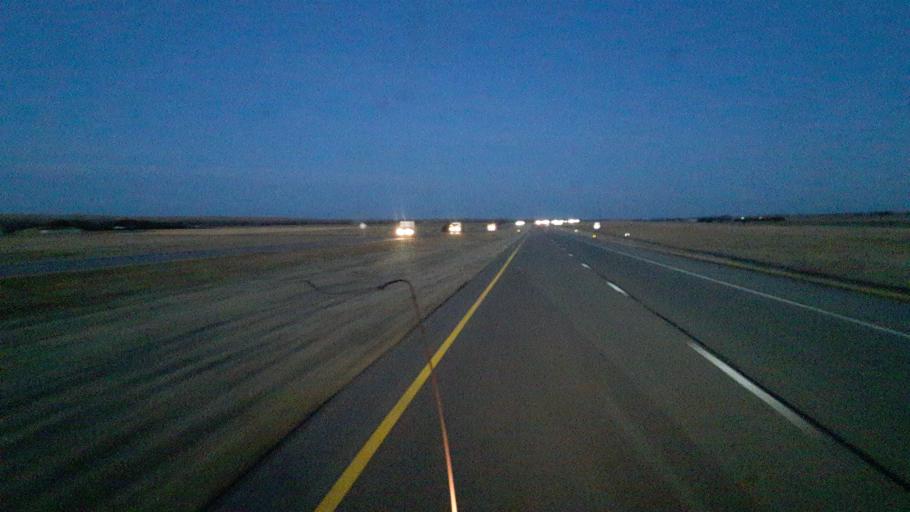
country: US
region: Nebraska
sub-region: Lincoln County
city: Sutherland
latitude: 41.1120
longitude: -101.3461
